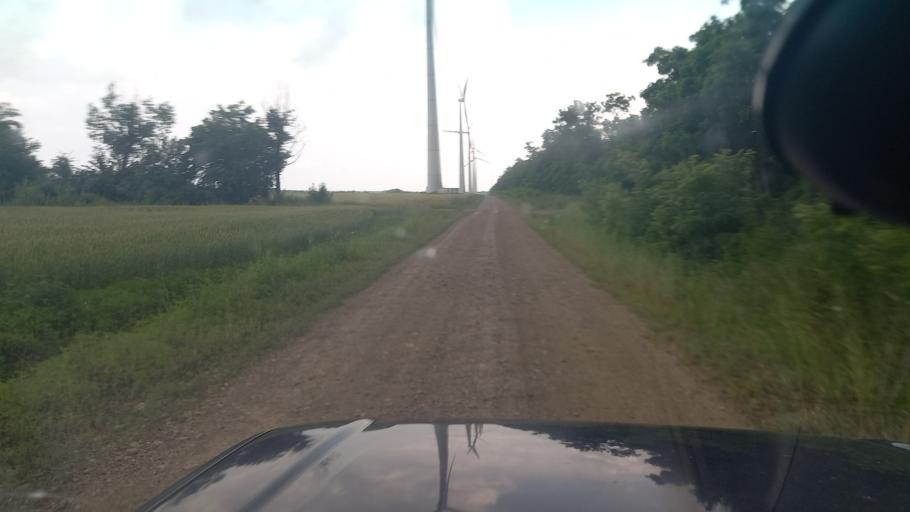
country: RU
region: Adygeya
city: Shovgenovskiy
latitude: 44.9704
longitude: 40.1340
